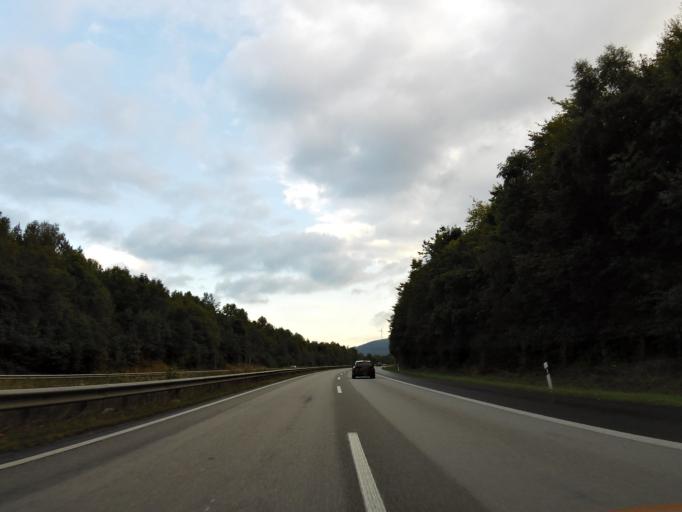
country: DE
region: Rheinland-Pfalz
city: Rheinbollen
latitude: 50.0174
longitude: 7.6812
